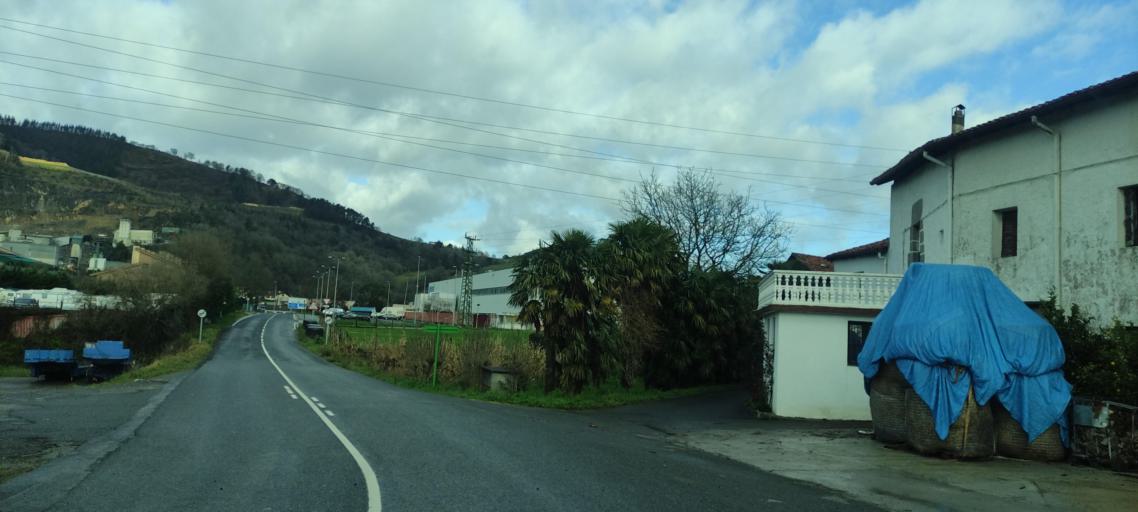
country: ES
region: Basque Country
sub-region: Provincia de Guipuzcoa
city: Urnieta
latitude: 43.2335
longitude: -1.9967
